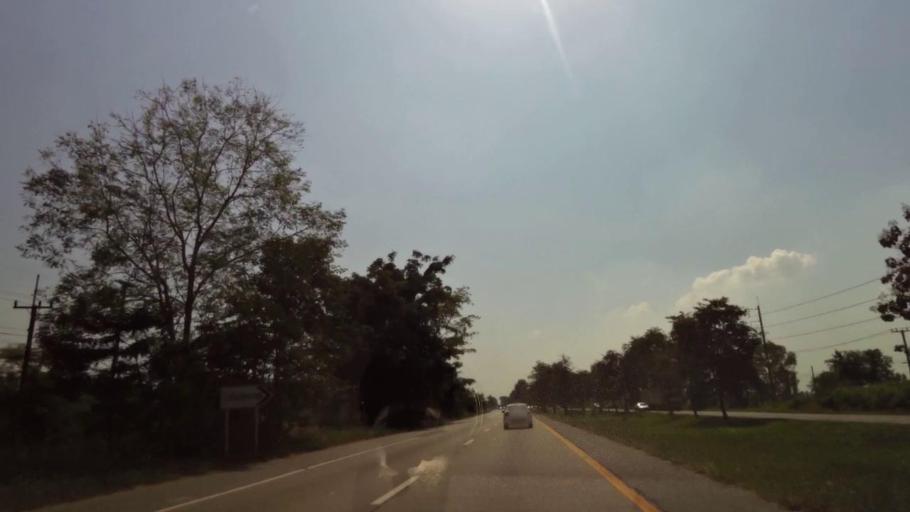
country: TH
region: Phichit
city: Wachira Barami
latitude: 16.5880
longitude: 100.1471
